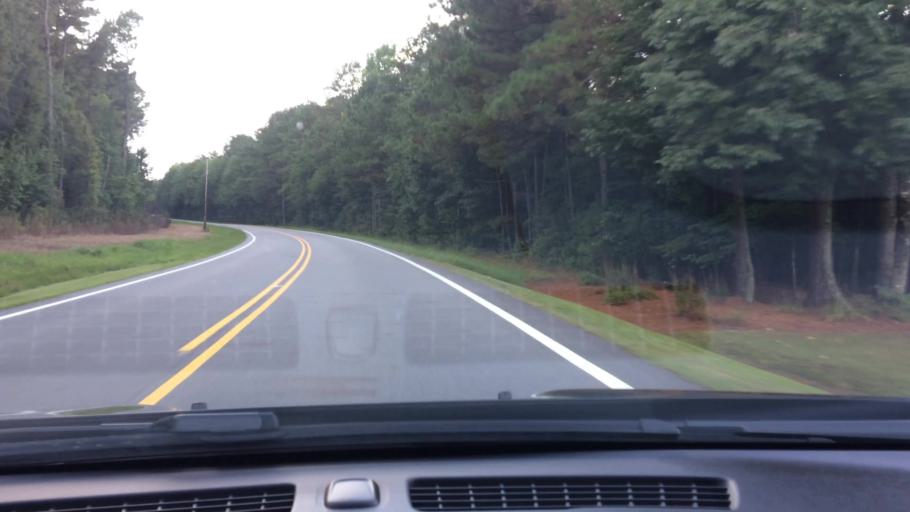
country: US
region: North Carolina
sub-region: Craven County
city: Vanceboro
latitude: 35.4278
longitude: -77.2102
